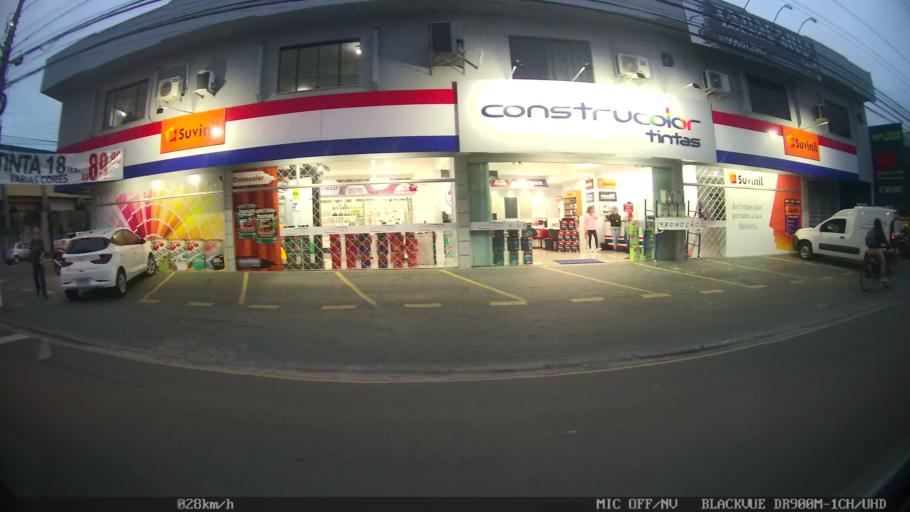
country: BR
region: Santa Catarina
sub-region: Itajai
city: Itajai
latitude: -26.9033
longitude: -48.6693
